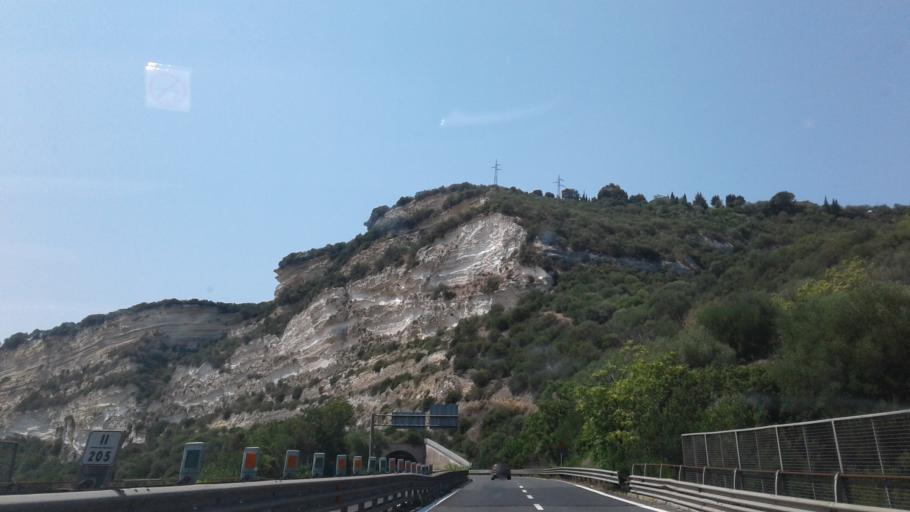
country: IT
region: Sardinia
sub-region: Provincia di Sassari
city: Ossi
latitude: 40.7004
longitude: 8.5908
